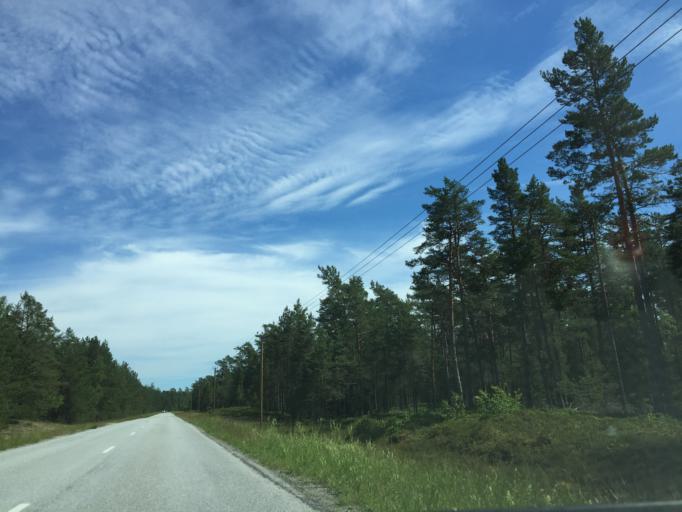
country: LV
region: Rojas
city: Roja
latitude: 57.5722
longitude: 22.6384
